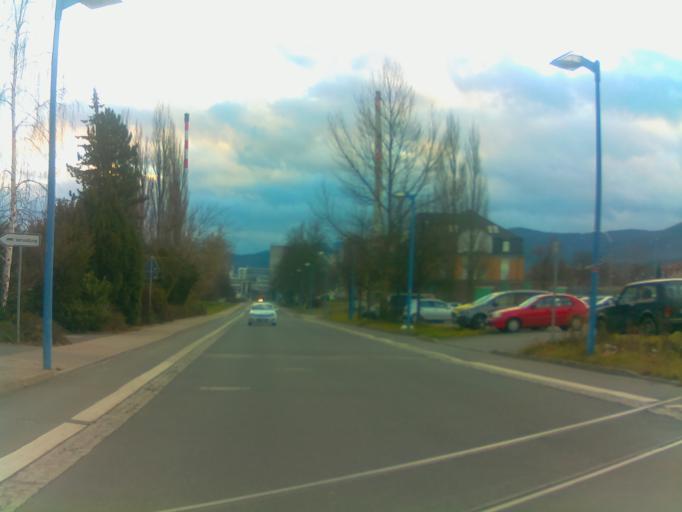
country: DE
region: Thuringia
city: Rudolstadt
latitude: 50.6933
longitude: 11.3295
